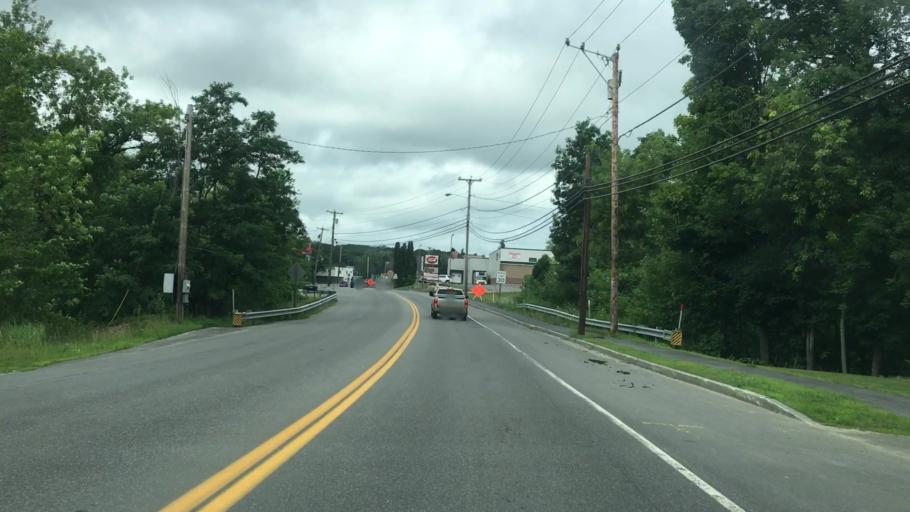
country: US
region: Maine
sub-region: Kennebec County
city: Randolph
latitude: 44.2279
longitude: -69.7637
